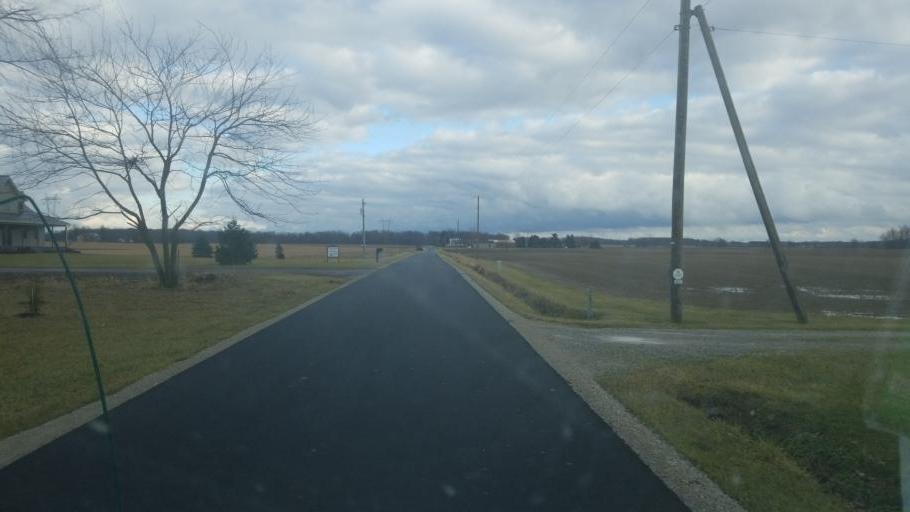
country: US
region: Ohio
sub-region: Crawford County
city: Galion
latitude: 40.7122
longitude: -82.8731
